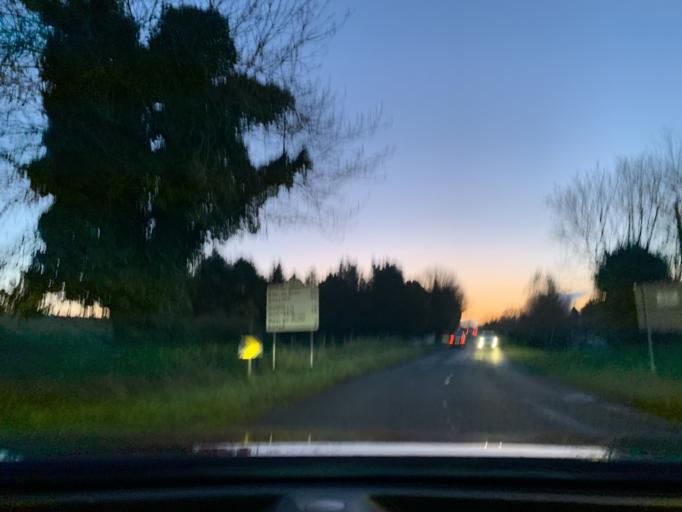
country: IE
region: Connaught
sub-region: Roscommon
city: Boyle
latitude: 53.9692
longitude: -8.2631
